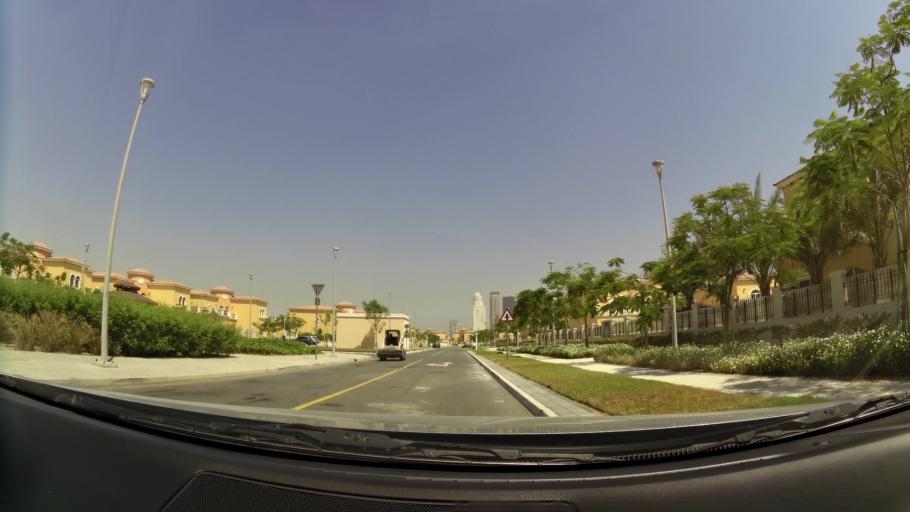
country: AE
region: Dubai
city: Dubai
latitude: 25.0534
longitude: 55.1482
